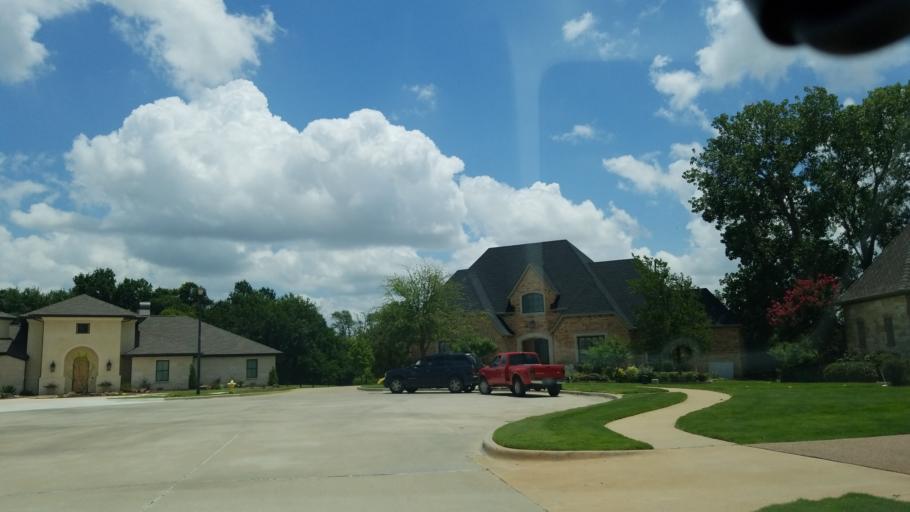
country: US
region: Texas
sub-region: Dallas County
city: Carrollton
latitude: 32.9642
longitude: -96.9454
